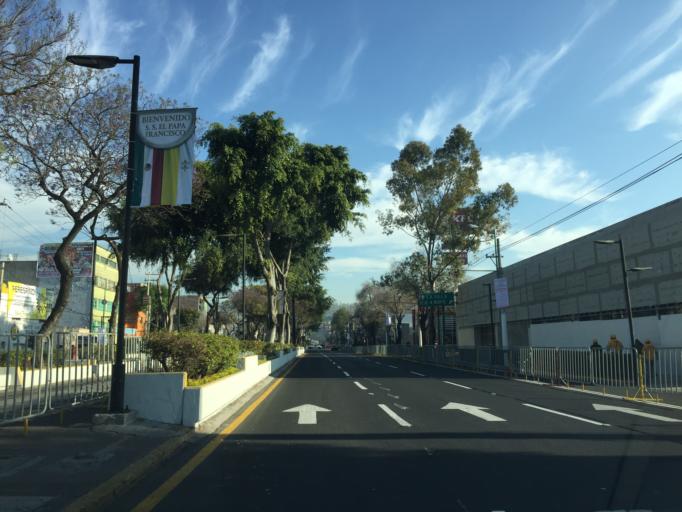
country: MX
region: Mexico
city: Colonia Lindavista
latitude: 19.4766
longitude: -99.1203
